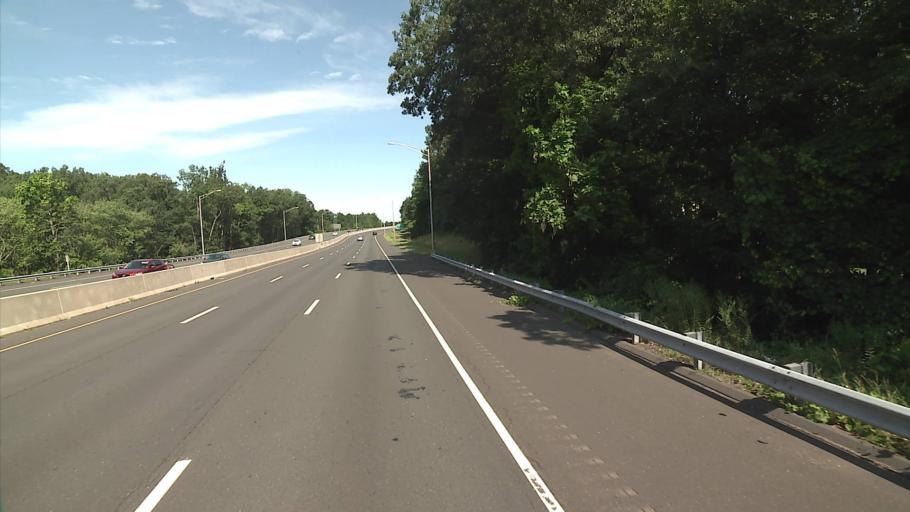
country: US
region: Connecticut
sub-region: Hartford County
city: Glastonbury
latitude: 41.7193
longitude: -72.6031
